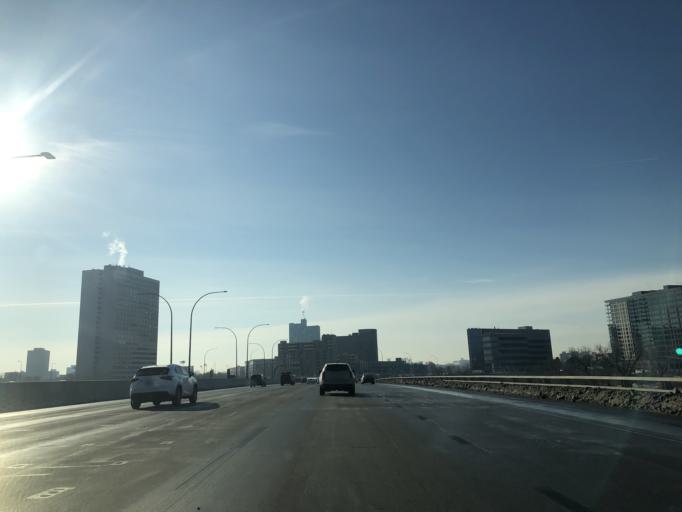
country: US
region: Minnesota
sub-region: Hennepin County
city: Minneapolis
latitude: 44.9768
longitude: -93.2439
